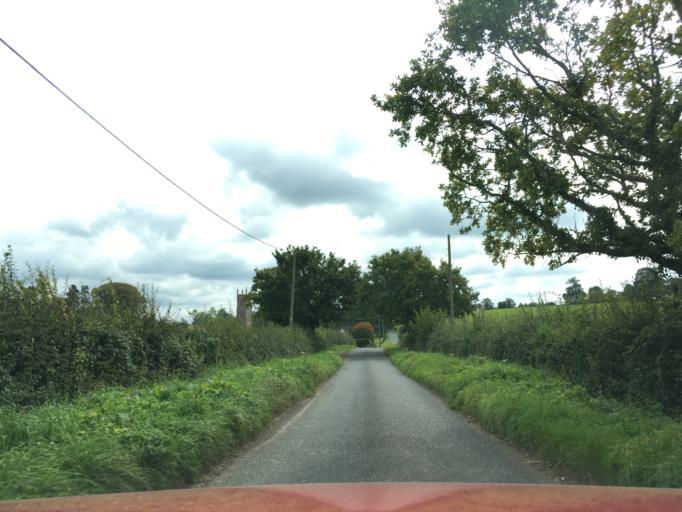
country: GB
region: England
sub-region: South Gloucestershire
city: Charfield
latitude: 51.6408
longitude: -2.4307
